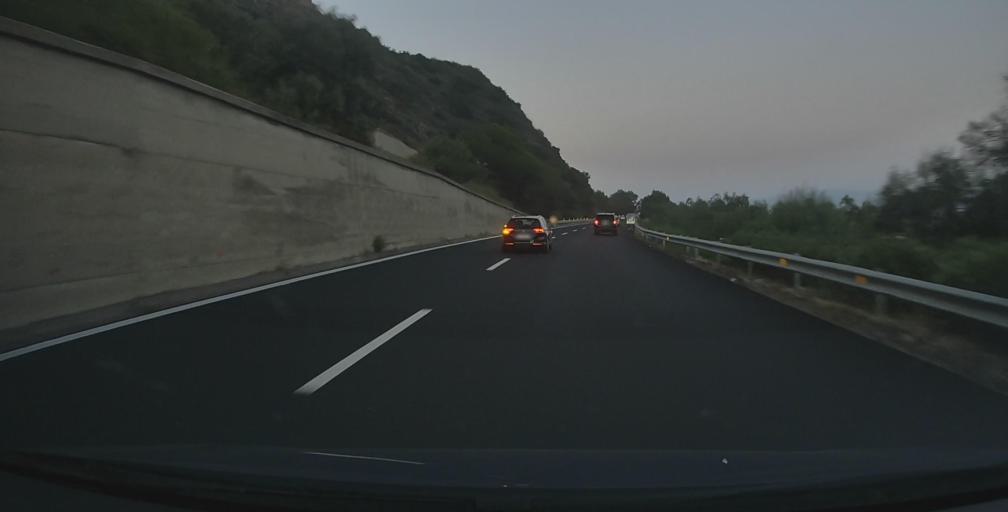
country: IT
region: Sicily
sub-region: Messina
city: Scaletta Zanclea
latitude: 38.0673
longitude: 15.4818
